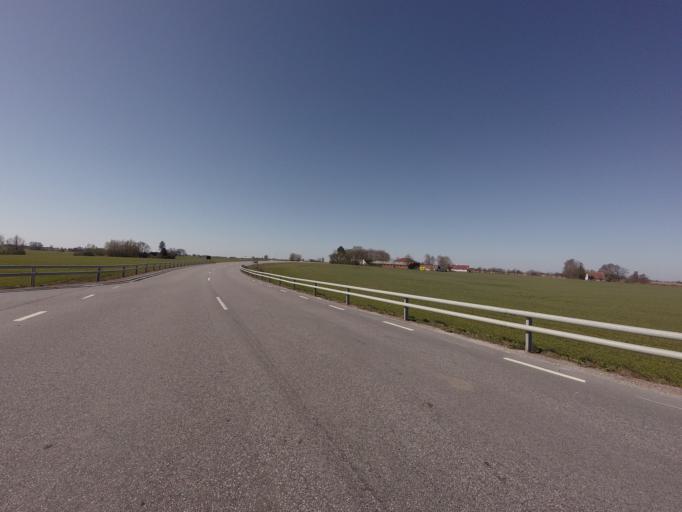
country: SE
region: Skane
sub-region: Malmo
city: Oxie
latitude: 55.4714
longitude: 13.1271
